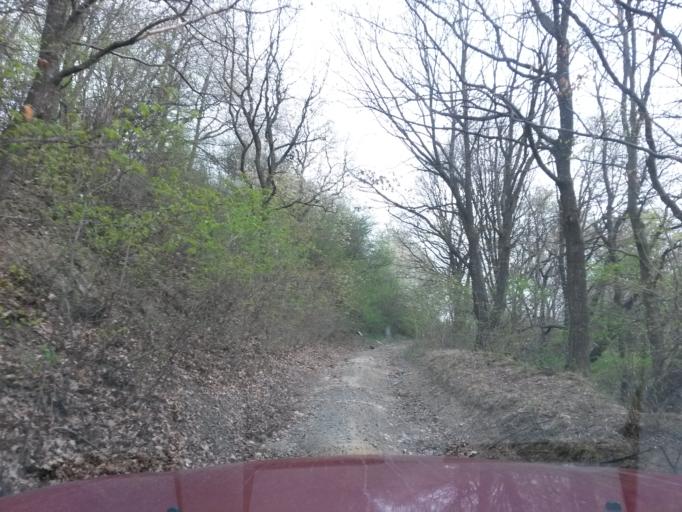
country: SK
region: Kosicky
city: Kosice
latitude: 48.7423
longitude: 21.1194
